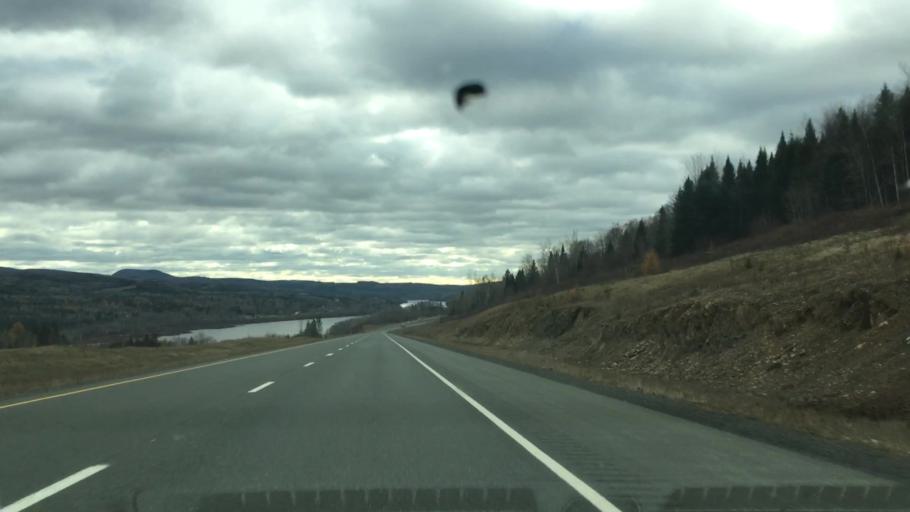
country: US
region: Maine
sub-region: Aroostook County
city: Fort Fairfield
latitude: 46.6867
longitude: -67.7353
